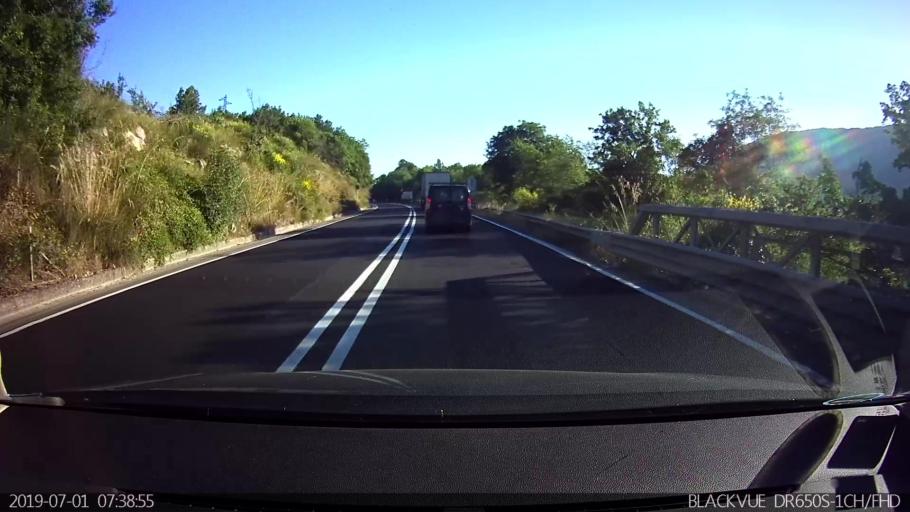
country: IT
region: Latium
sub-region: Provincia di Frosinone
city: Giuliano di Roma
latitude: 41.5461
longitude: 13.2695
